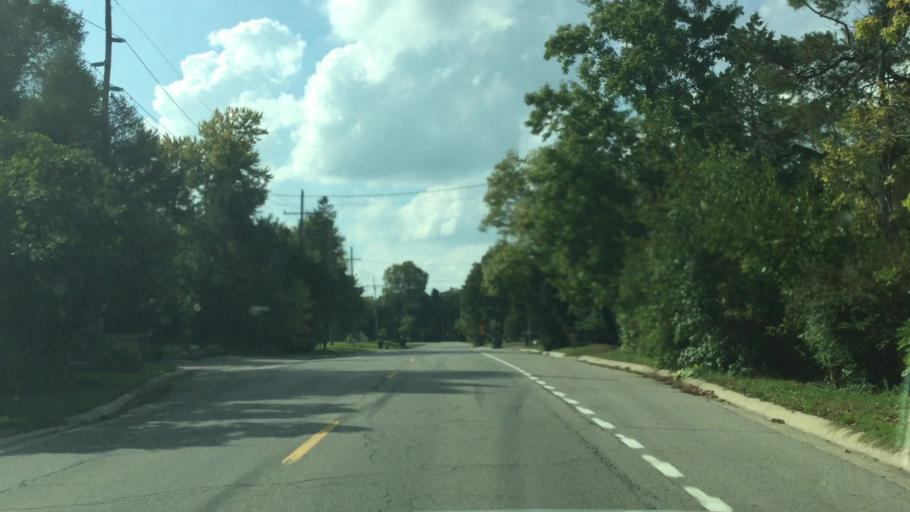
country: US
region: Michigan
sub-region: Oakland County
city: Waterford
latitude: 42.6523
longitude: -83.4151
